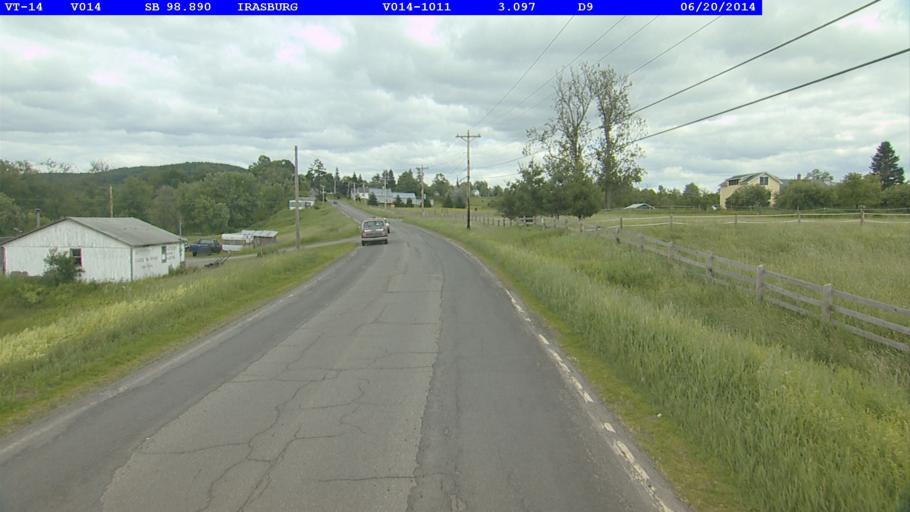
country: US
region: Vermont
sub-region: Orleans County
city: Newport
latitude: 44.8072
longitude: -72.2852
